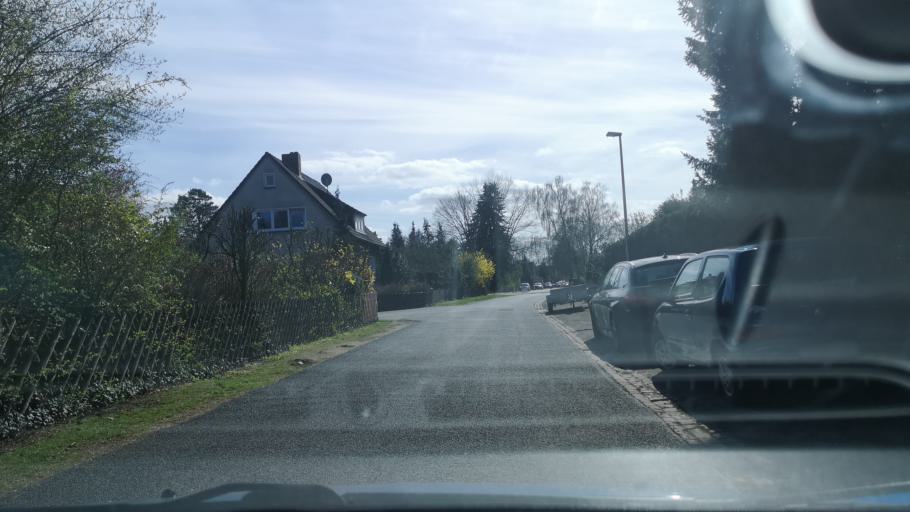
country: DE
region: Lower Saxony
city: Langenhagen
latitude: 52.4366
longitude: 9.7934
